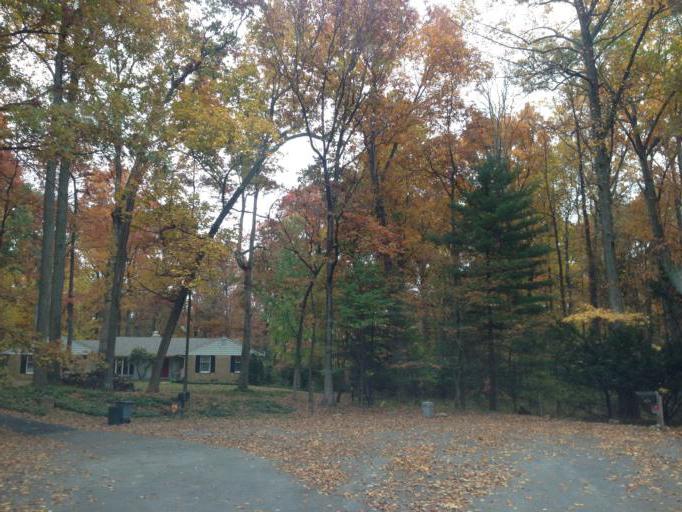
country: US
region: Maryland
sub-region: Howard County
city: Highland
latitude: 39.2766
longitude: -76.9412
